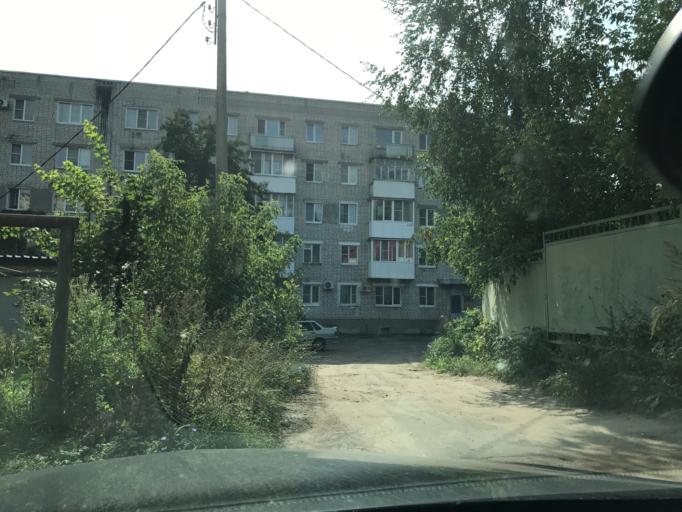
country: RU
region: Nizjnij Novgorod
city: Taremskoye
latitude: 55.9551
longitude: 43.0549
